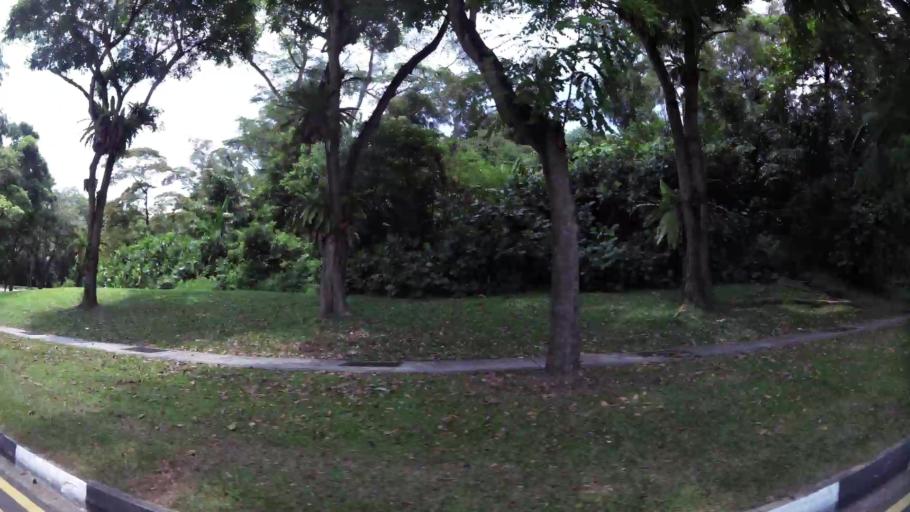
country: MY
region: Johor
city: Johor Bahru
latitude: 1.4272
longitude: 103.7638
